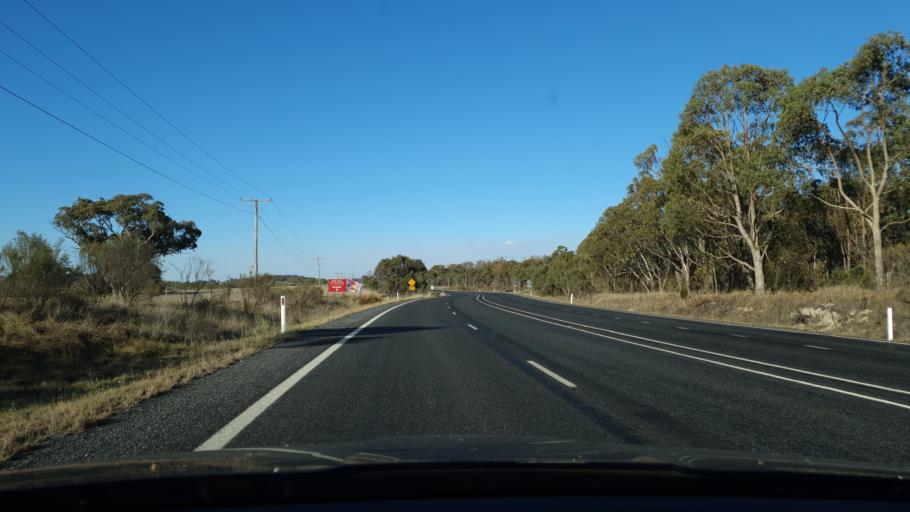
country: AU
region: Queensland
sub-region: Southern Downs
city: Stanthorpe
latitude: -28.6904
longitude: 151.9089
